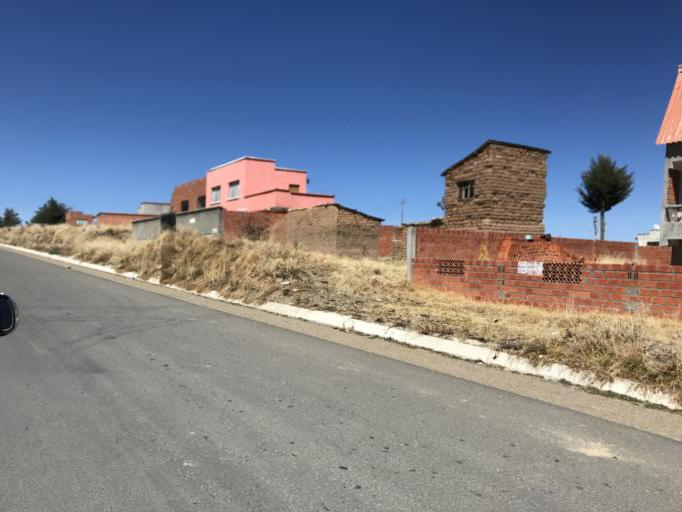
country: BO
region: La Paz
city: Huatajata
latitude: -16.1935
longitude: -68.7292
